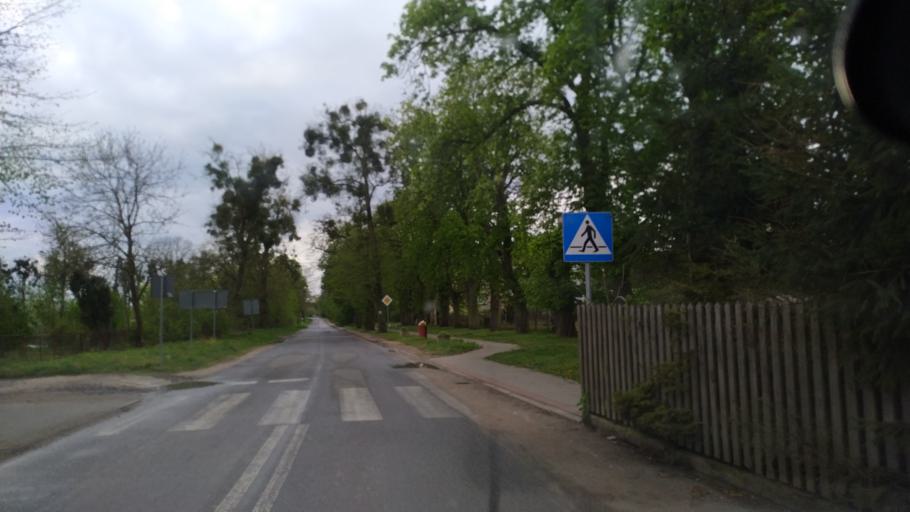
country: PL
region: Pomeranian Voivodeship
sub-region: Powiat starogardzki
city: Smetowo Graniczne
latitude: 53.7371
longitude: 18.6490
